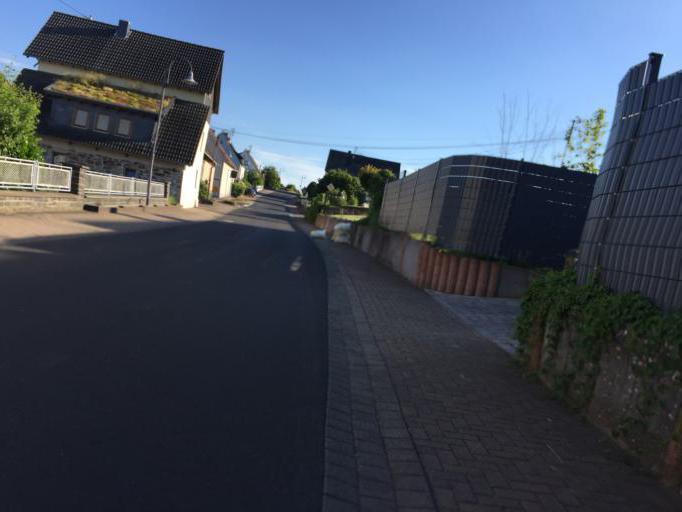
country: DE
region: Rheinland-Pfalz
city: Hartlingen
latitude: 50.5284
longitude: 7.9101
